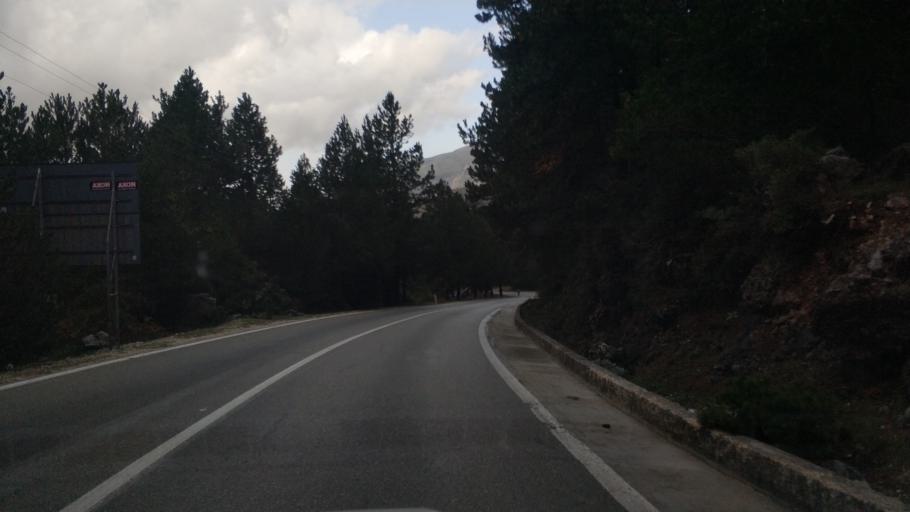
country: AL
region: Vlore
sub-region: Rrethi i Vlores
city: Brataj
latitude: 40.2231
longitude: 19.5785
